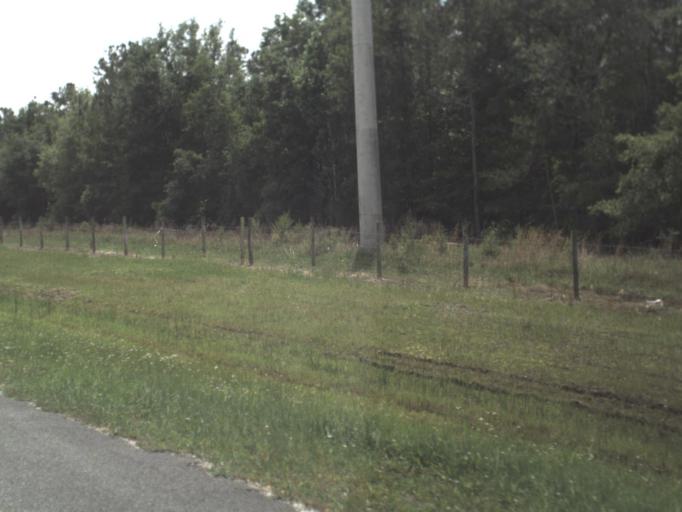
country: US
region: Florida
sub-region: Clay County
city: Asbury Lake
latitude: 29.9080
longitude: -81.8975
